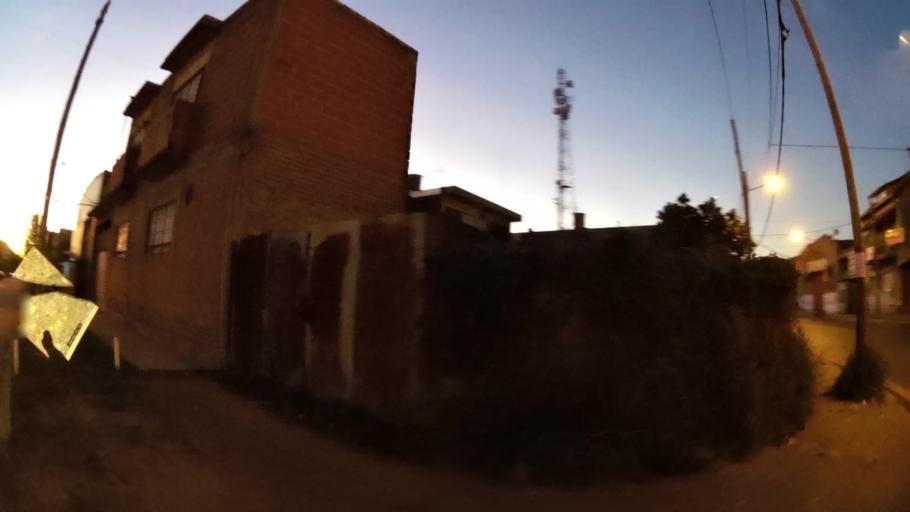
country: AR
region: Buenos Aires
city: San Justo
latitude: -34.7094
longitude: -58.5857
